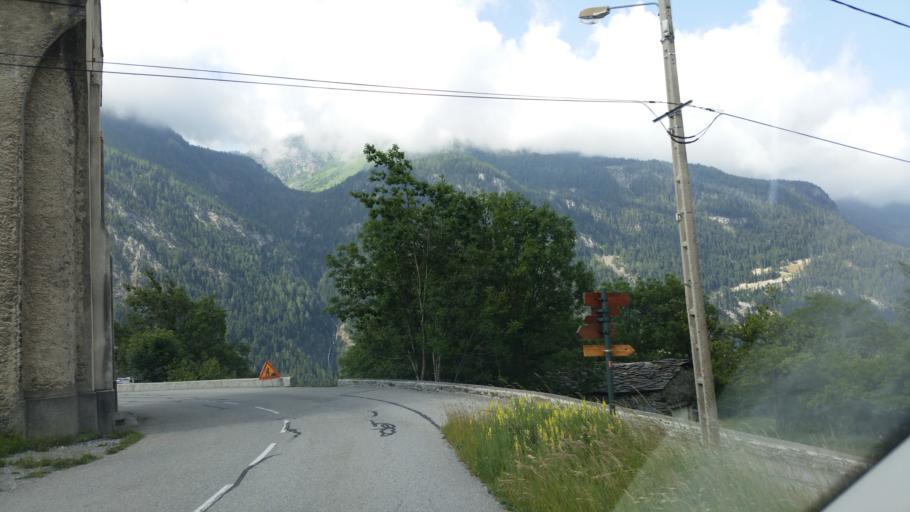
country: FR
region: Rhone-Alpes
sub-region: Departement de la Savoie
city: Modane
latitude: 45.2087
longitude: 6.5969
